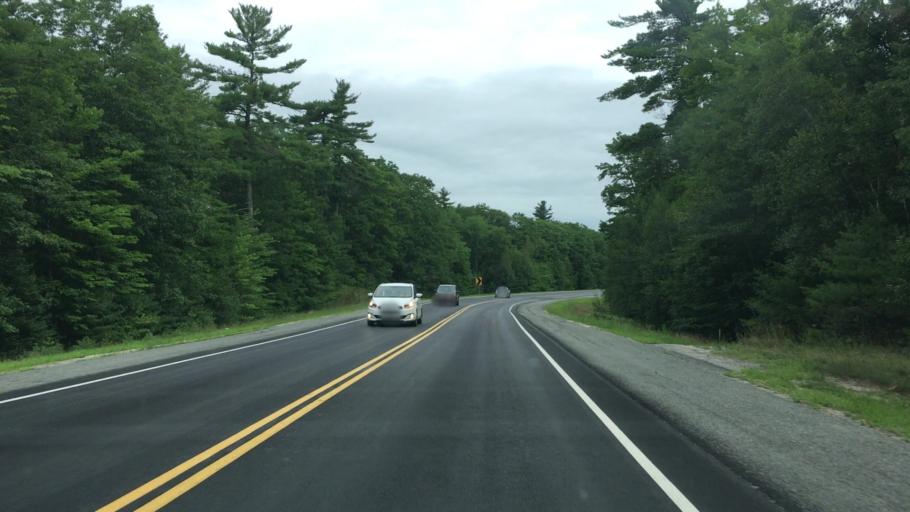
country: US
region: Maine
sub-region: Washington County
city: Cherryfield
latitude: 44.9062
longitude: -67.8569
